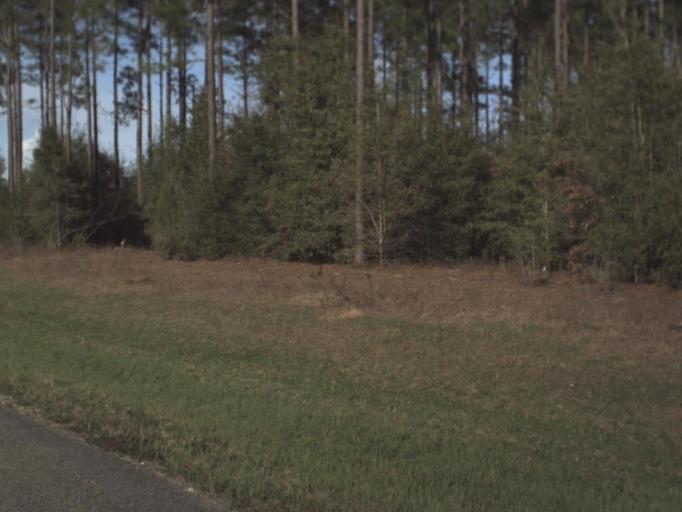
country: US
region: Florida
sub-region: Jackson County
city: Marianna
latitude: 30.5928
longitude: -85.1816
